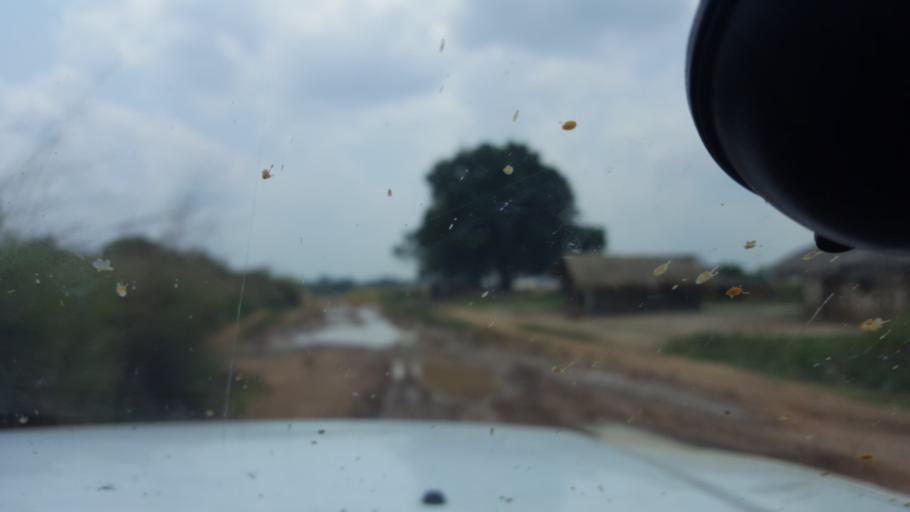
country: CD
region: Bandundu
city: Mushie
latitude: -3.7475
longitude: 16.6494
